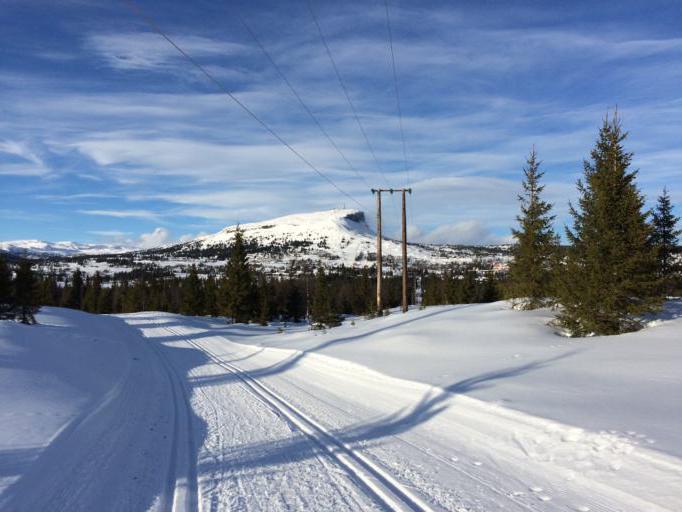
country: NO
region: Oppland
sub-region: Gausdal
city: Segalstad bru
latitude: 61.3224
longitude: 10.0811
